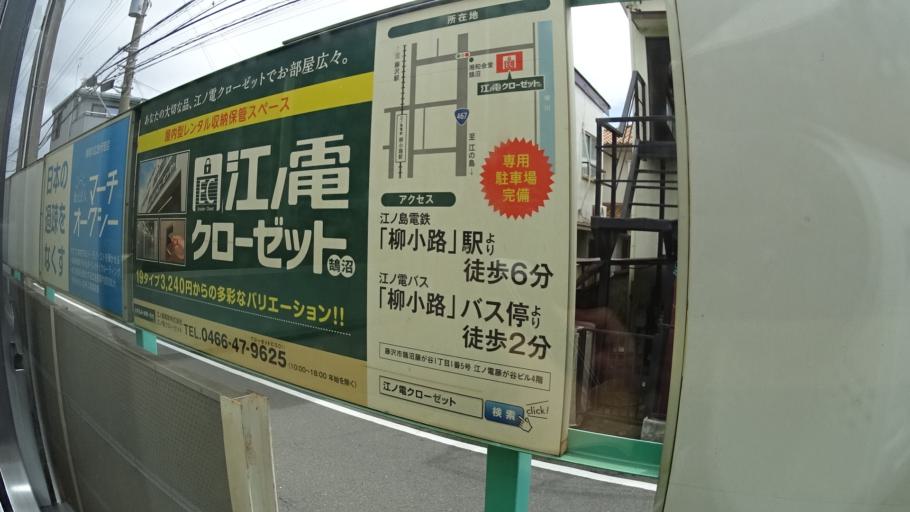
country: JP
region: Kanagawa
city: Fujisawa
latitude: 35.3273
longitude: 139.4853
